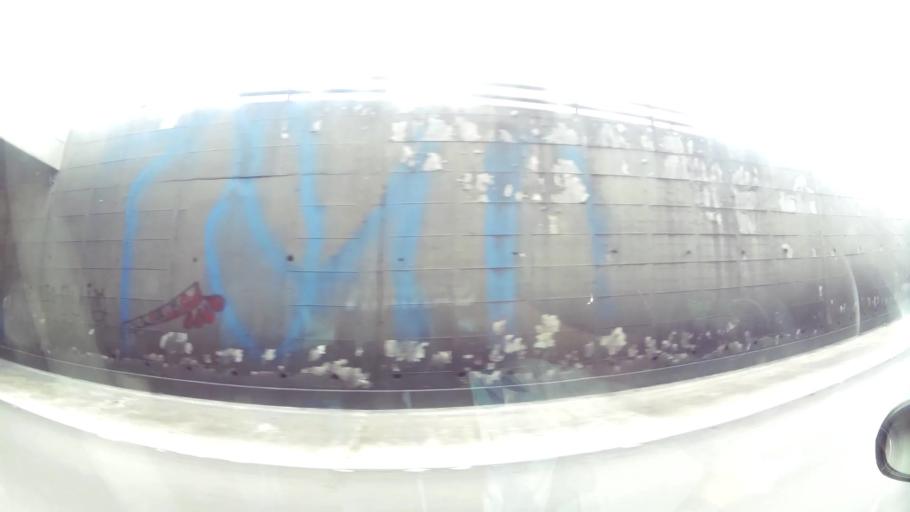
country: EC
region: Pichincha
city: Quito
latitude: -0.2013
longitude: -78.5013
